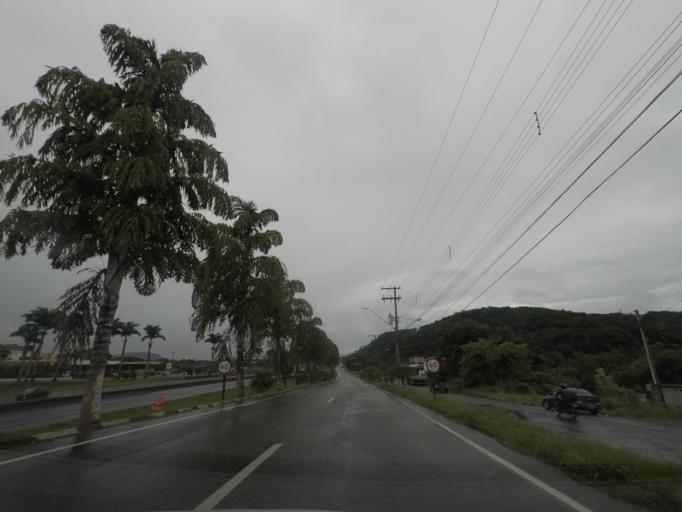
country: BR
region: Sao Paulo
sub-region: Jacupiranga
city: Jacupiranga
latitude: -24.6972
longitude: -48.0007
